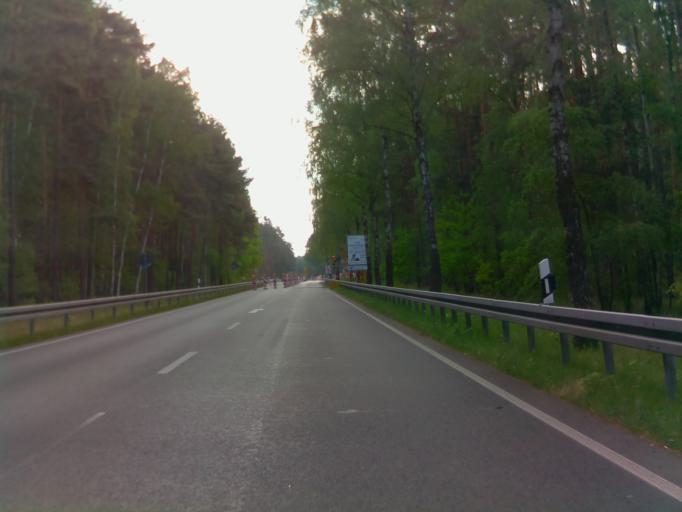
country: DE
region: Saxony-Anhalt
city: Schollene
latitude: 52.5726
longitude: 12.2051
